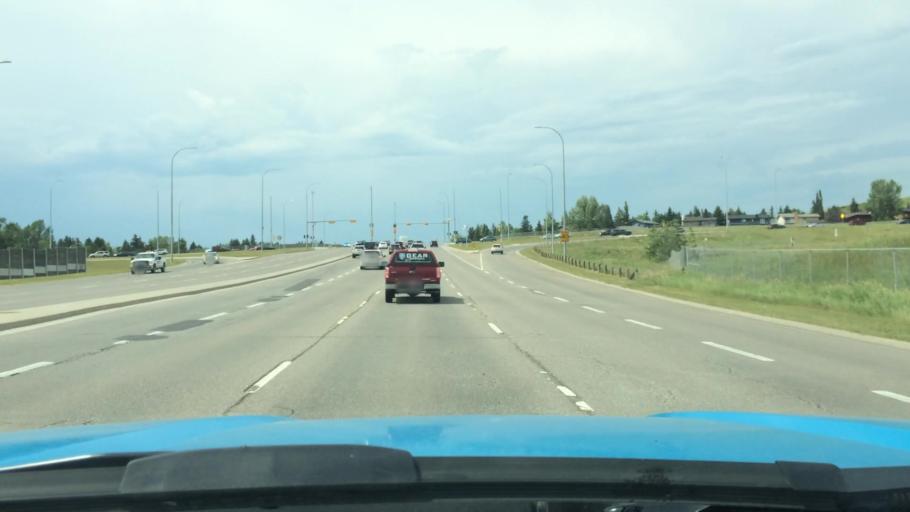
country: CA
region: Alberta
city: Calgary
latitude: 51.1082
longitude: -114.1372
